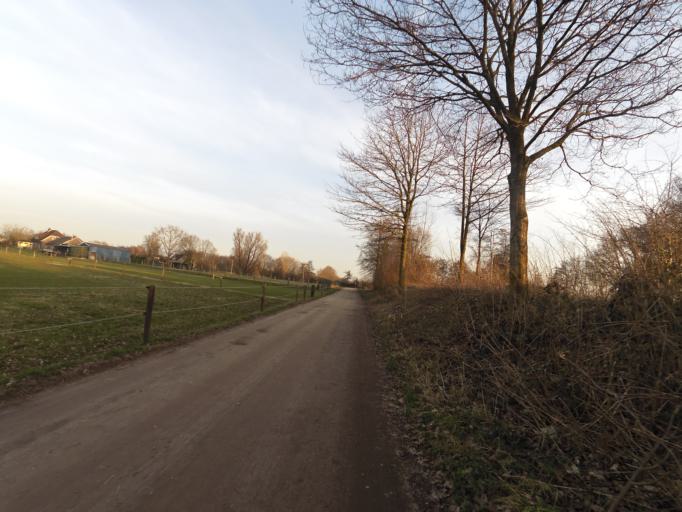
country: NL
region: Gelderland
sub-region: Gemeente Zevenaar
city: Zevenaar
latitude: 51.9430
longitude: 6.1140
